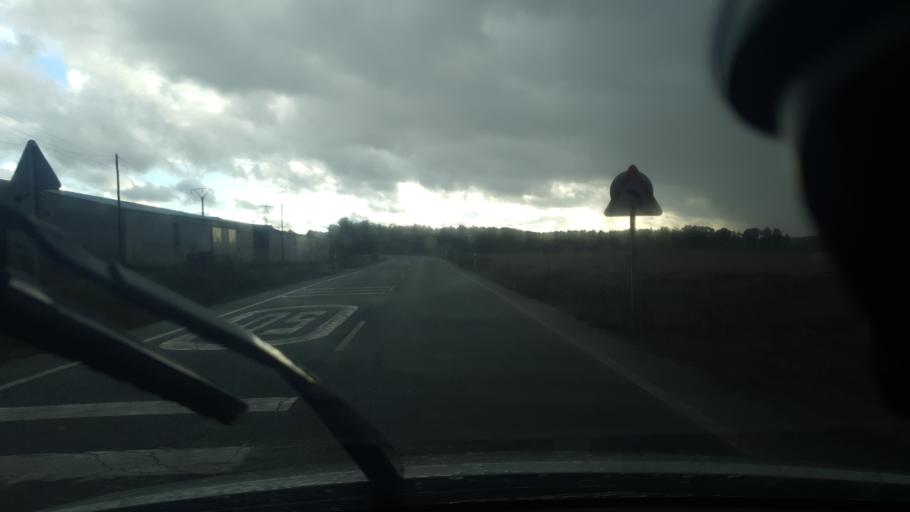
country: ES
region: Castille and Leon
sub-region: Provincia de Segovia
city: Samboal
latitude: 41.2973
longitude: -4.4089
